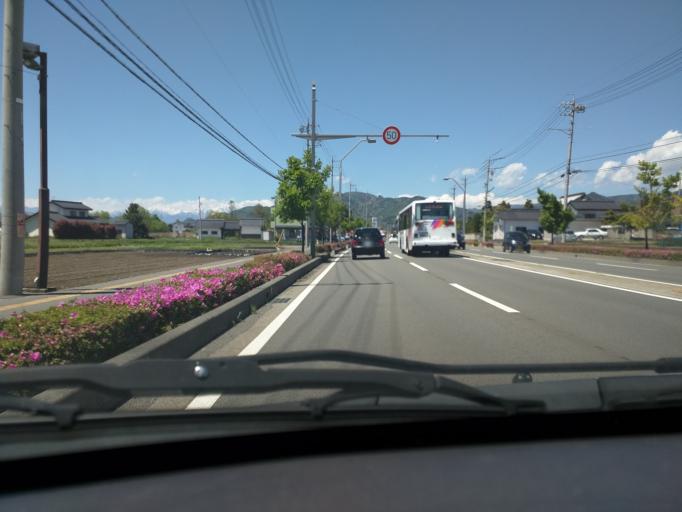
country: JP
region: Nagano
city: Nagano-shi
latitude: 36.6424
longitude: 138.2332
